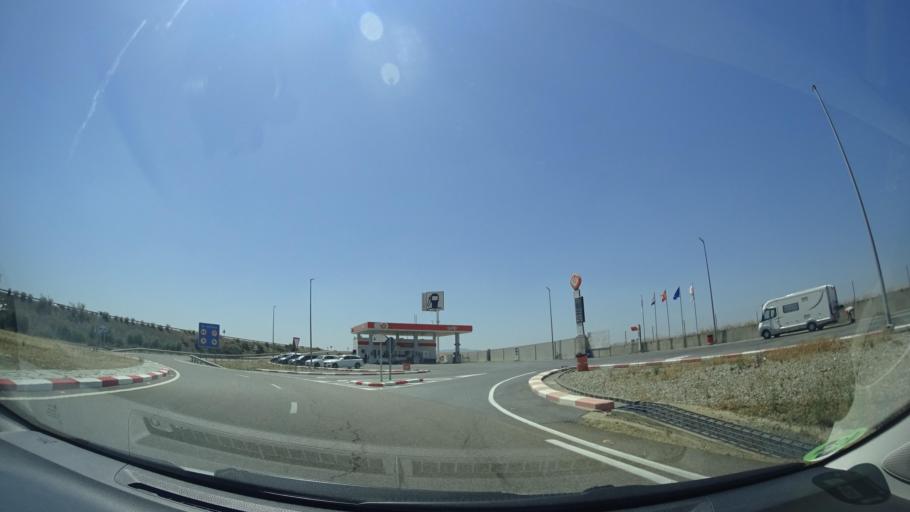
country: ES
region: Extremadura
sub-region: Provincia de Badajoz
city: Fuente de Cantos
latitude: 38.2308
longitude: -6.2967
